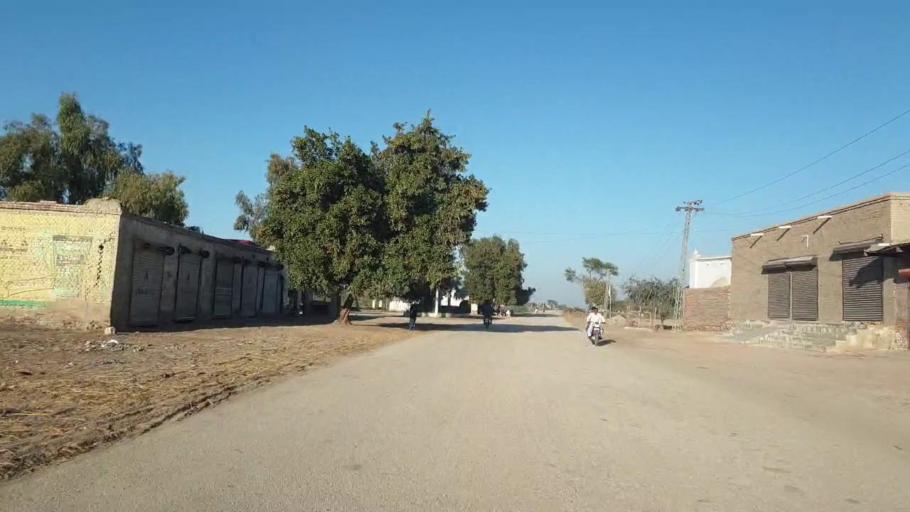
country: PK
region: Sindh
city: Dokri
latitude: 27.3683
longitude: 68.1166
